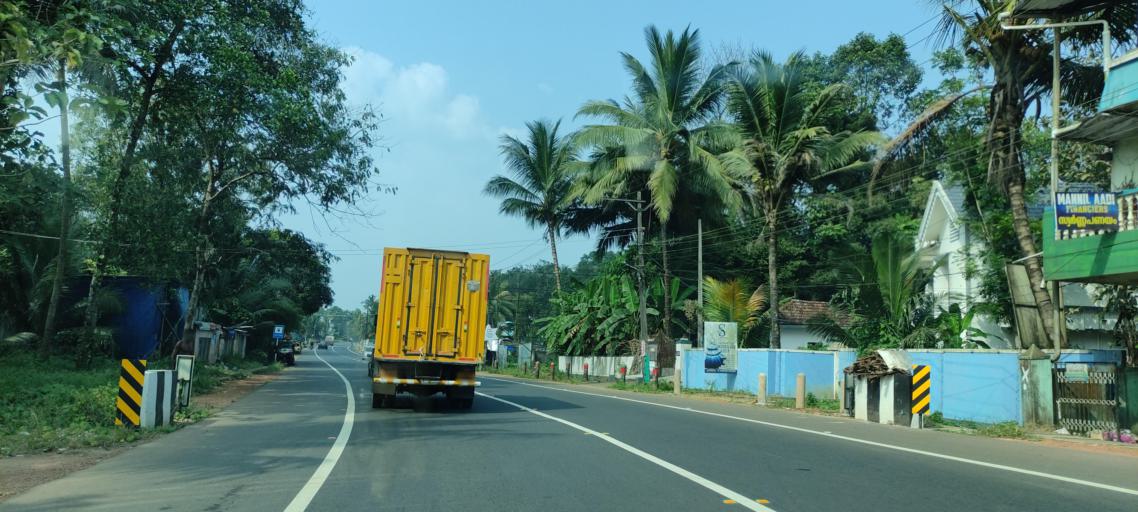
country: IN
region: Kerala
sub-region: Alappuzha
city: Chengannur
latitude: 9.2790
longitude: 76.6557
